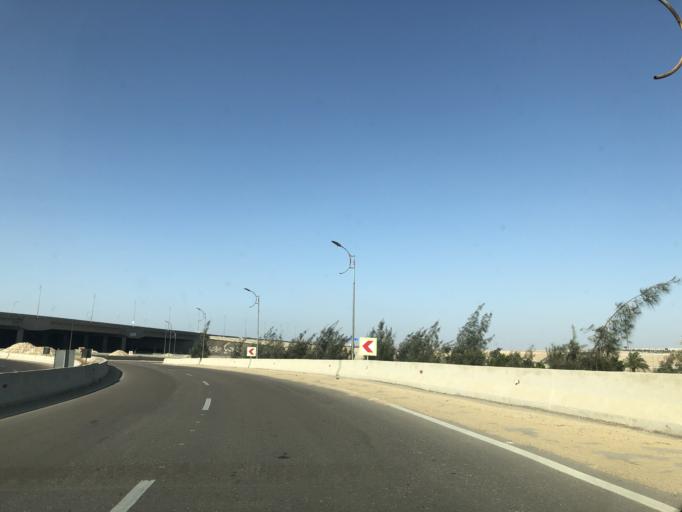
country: EG
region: Al Jizah
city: Awsim
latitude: 30.0736
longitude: 30.9262
